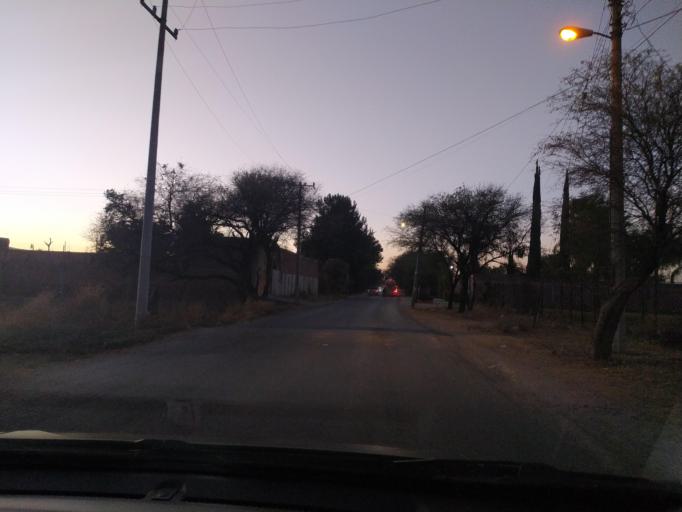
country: MX
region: Guanajuato
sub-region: San Francisco del Rincon
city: San Roque de Montes
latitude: 21.0176
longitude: -101.8214
